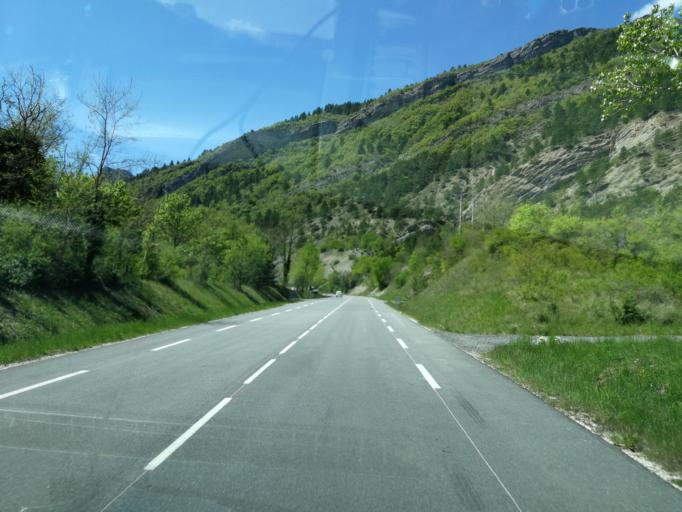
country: FR
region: Rhone-Alpes
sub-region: Departement de la Drome
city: Die
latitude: 44.6969
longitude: 5.2435
